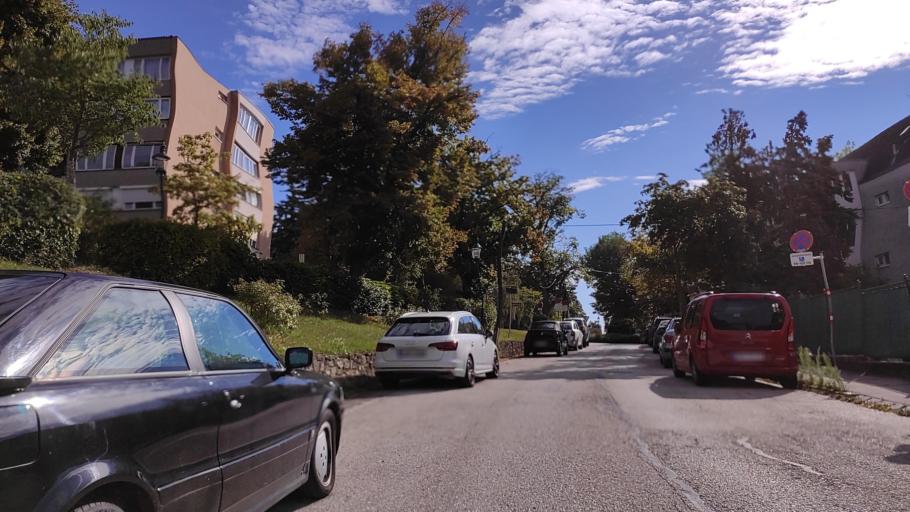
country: AT
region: Lower Austria
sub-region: Politischer Bezirk Baden
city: Baden
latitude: 48.0097
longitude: 16.2213
